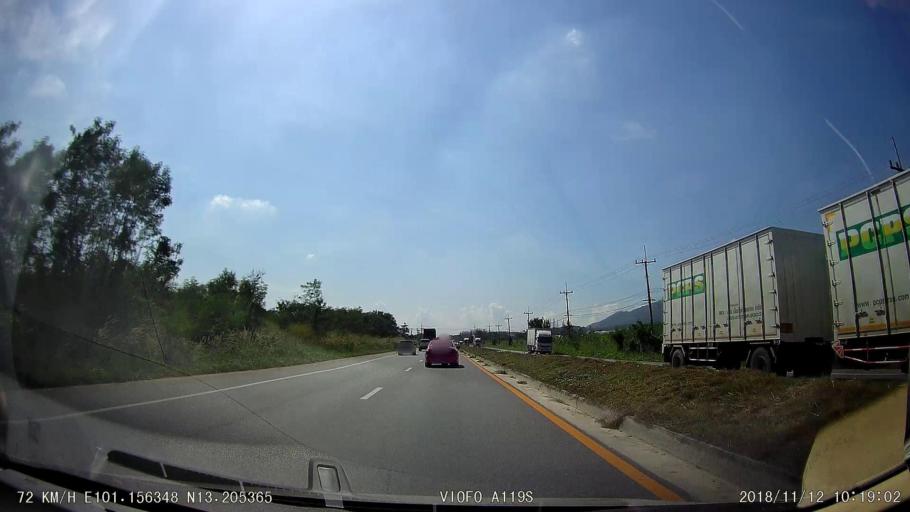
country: TH
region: Chon Buri
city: Ban Bueng
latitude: 13.2049
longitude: 101.1564
